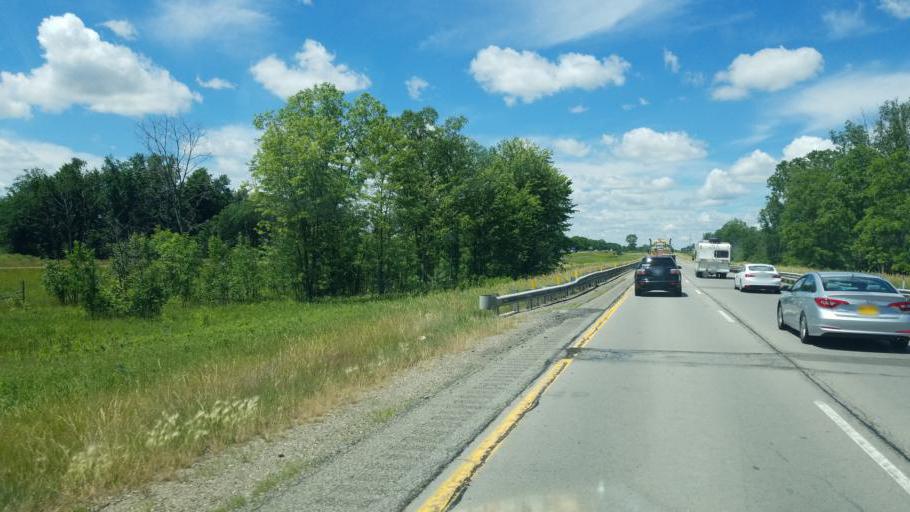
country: US
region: Michigan
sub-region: Livingston County
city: Fowlerville
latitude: 42.6465
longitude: -84.0802
